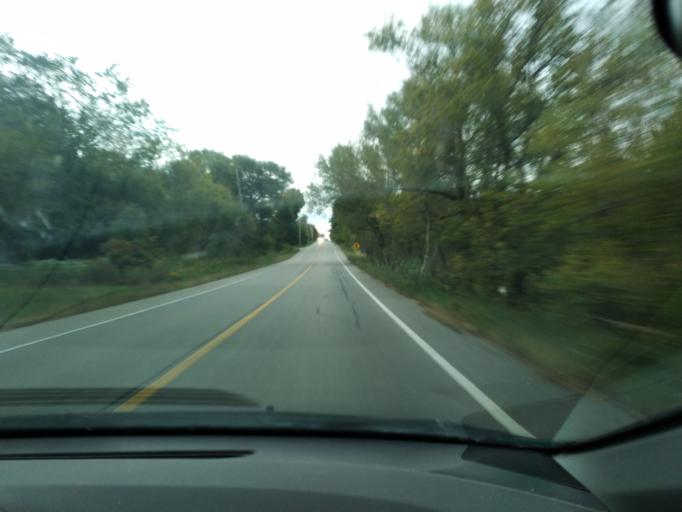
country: CA
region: Ontario
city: Bradford West Gwillimbury
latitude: 43.9636
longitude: -79.7820
